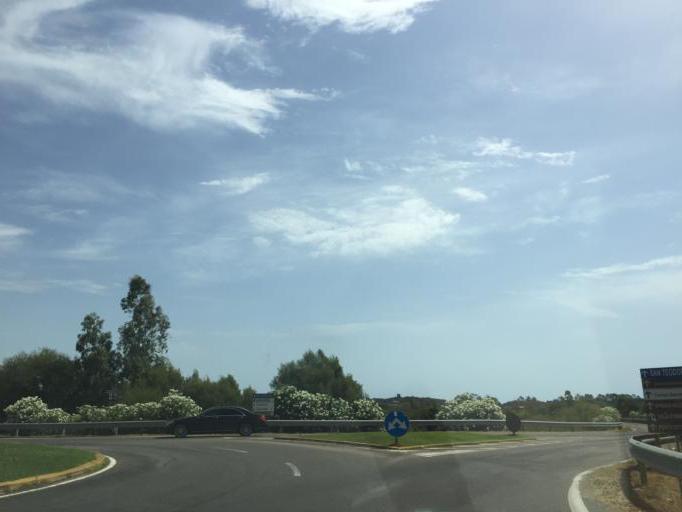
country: IT
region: Sardinia
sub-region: Provincia di Olbia-Tempio
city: San Teodoro
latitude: 40.7604
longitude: 9.6534
